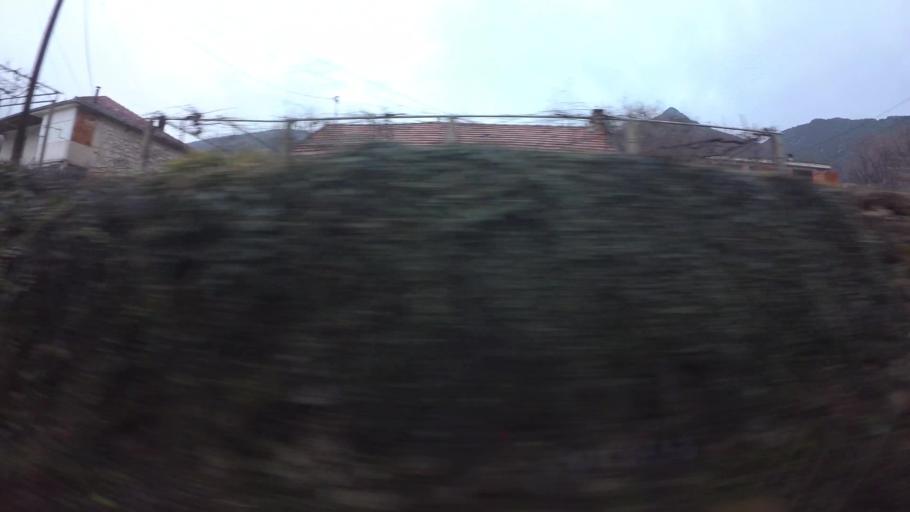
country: BA
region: Federation of Bosnia and Herzegovina
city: Cim
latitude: 43.3664
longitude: 17.8010
